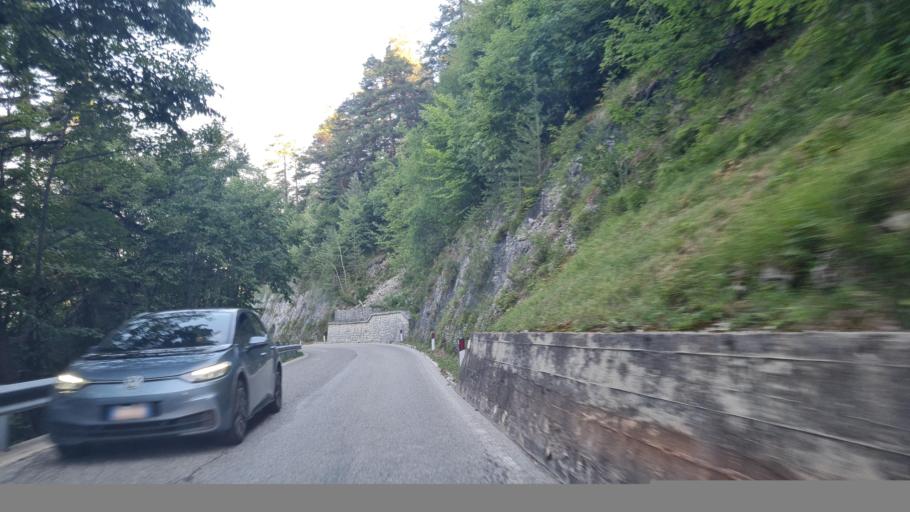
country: IT
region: Trentino-Alto Adige
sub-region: Provincia di Trento
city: Caldonazzo
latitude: 45.9713
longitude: 11.2916
